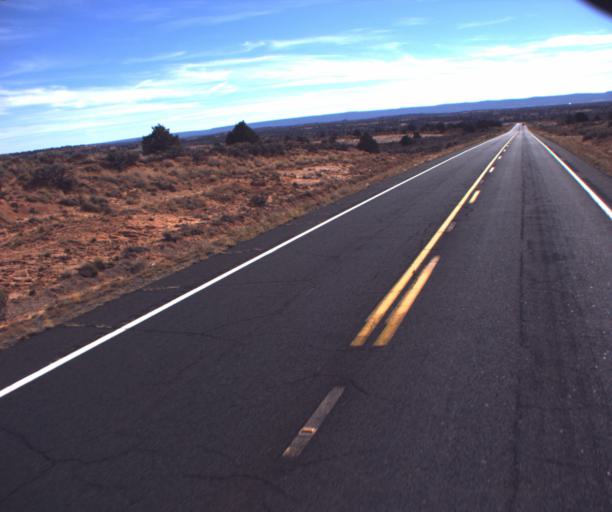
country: US
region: Arizona
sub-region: Coconino County
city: Kaibito
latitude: 36.5661
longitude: -110.7585
